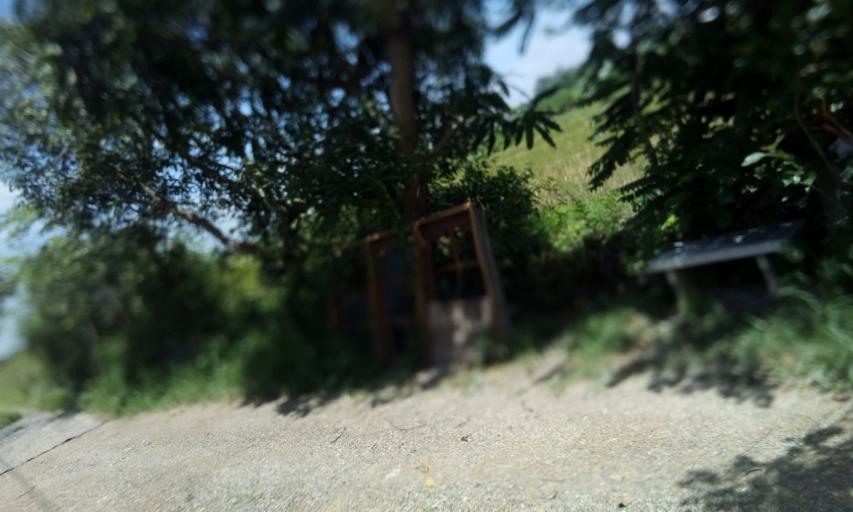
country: TH
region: Pathum Thani
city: Nong Suea
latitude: 14.0587
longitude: 100.8545
